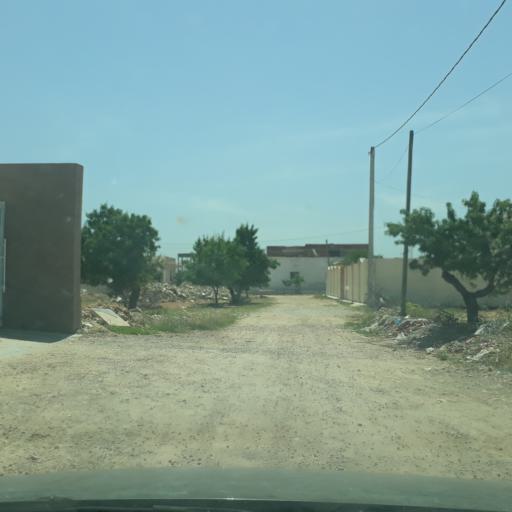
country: TN
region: Safaqis
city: Al Qarmadah
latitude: 34.8248
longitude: 10.7829
